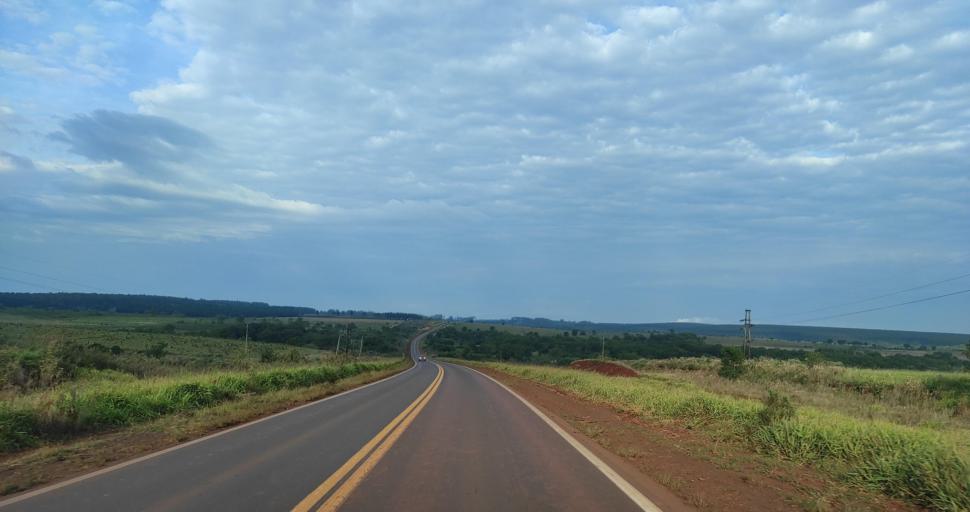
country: AR
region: Corrientes
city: Gobernador Ingeniero Valentin Virasoro
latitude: -27.9113
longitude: -55.9525
